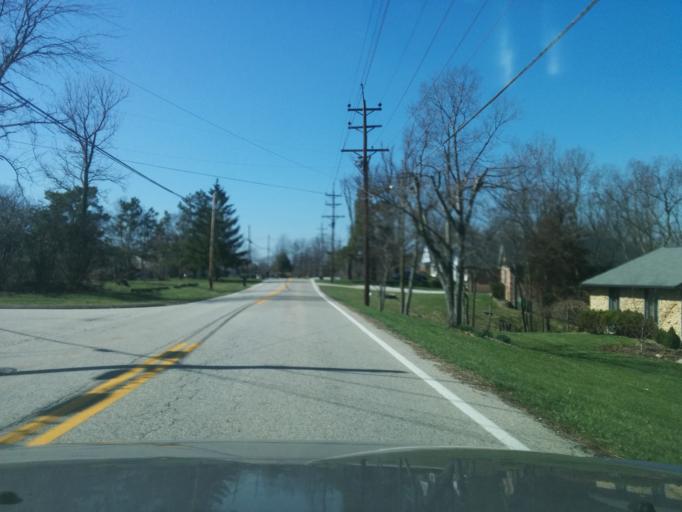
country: US
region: Ohio
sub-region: Hamilton County
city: Monfort Heights
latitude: 39.1817
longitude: -84.6124
